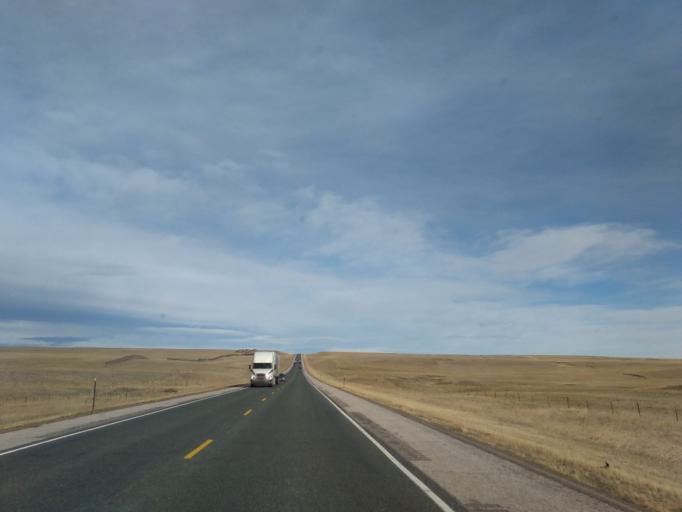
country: US
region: Wyoming
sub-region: Laramie County
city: Pine Bluffs
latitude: 41.5823
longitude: -104.2710
